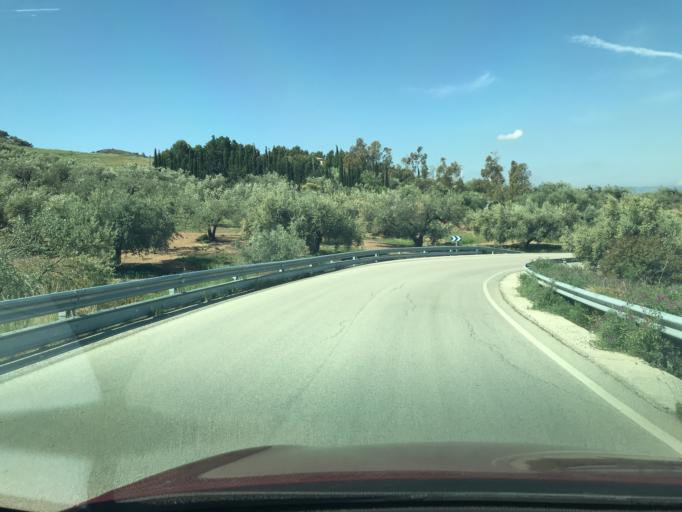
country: ES
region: Andalusia
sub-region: Provincia de Malaga
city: Alcaucin
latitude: 36.8975
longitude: -4.1245
